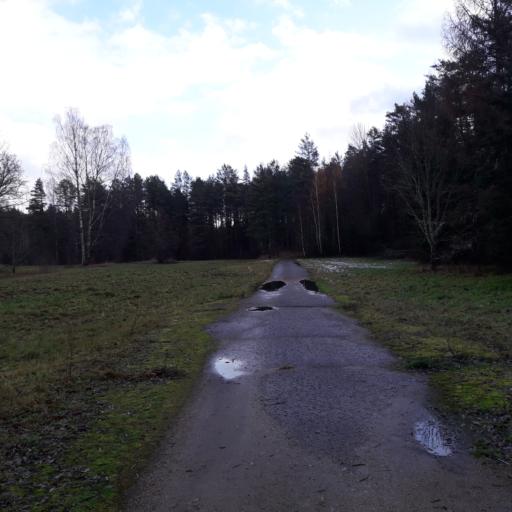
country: LV
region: Valmieras Rajons
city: Valmiera
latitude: 57.5433
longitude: 25.4585
